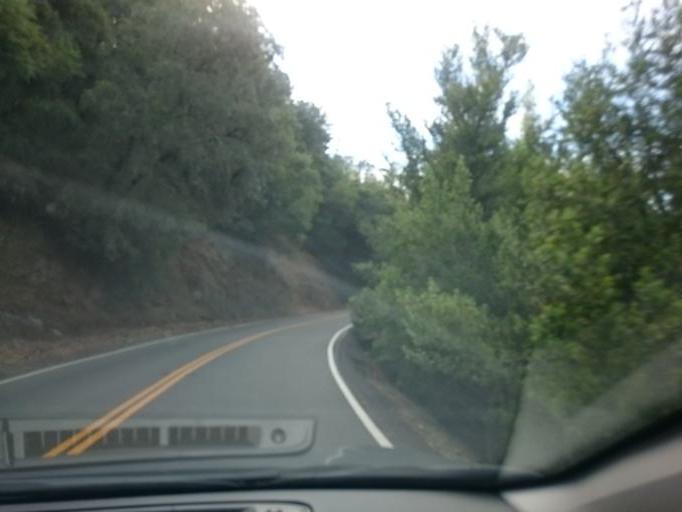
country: US
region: California
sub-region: Napa County
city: Yountville
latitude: 38.5020
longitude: -122.2957
